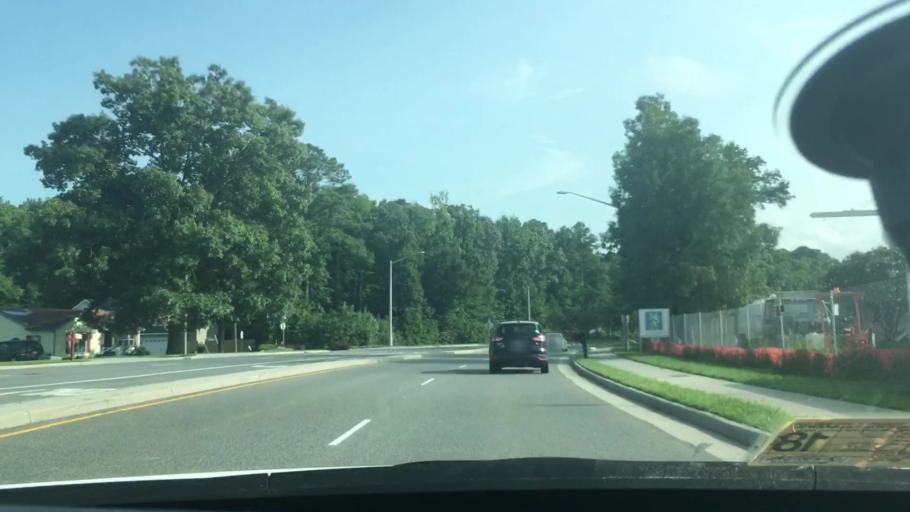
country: US
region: Virginia
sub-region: City of Virginia Beach
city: Virginia Beach
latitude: 36.8286
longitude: -75.9972
